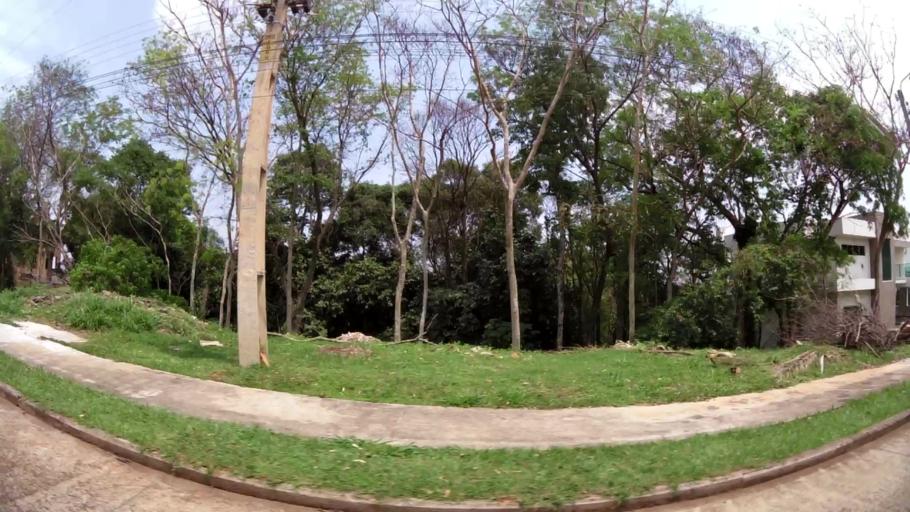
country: PY
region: Alto Parana
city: Ciudad del Este
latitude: -25.4979
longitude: -54.6081
